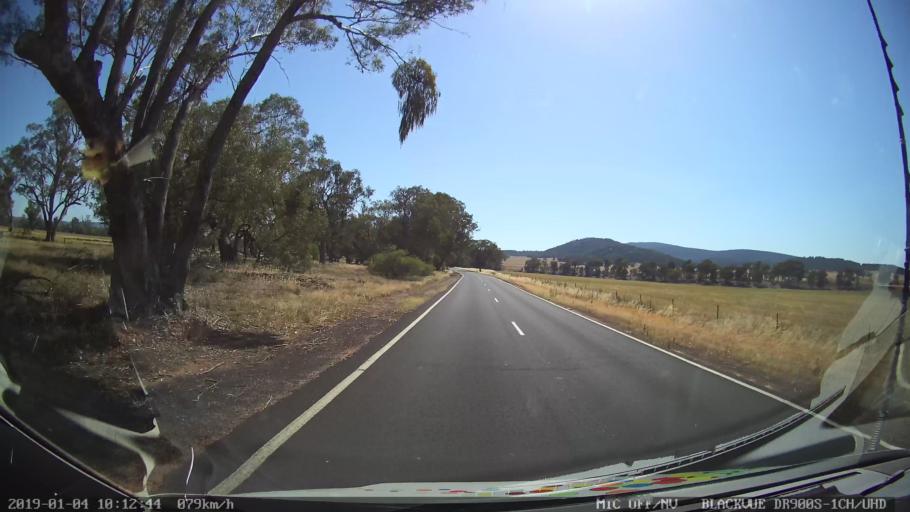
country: AU
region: New South Wales
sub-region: Cabonne
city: Canowindra
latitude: -33.4114
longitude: 148.3986
